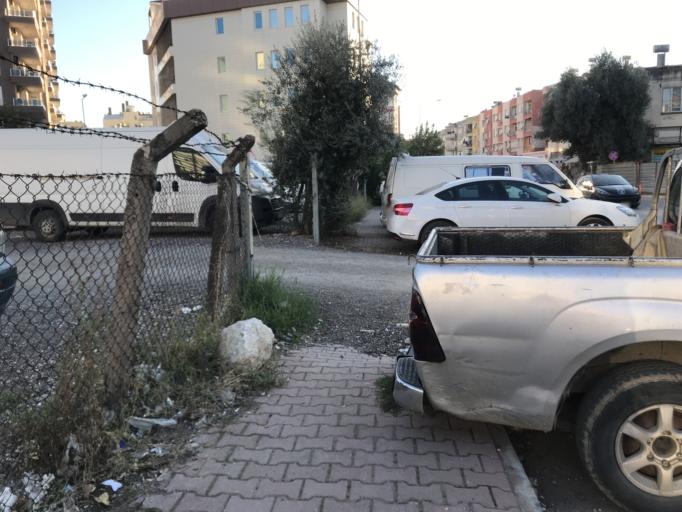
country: TR
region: Antalya
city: Antalya
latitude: 36.8980
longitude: 30.7076
